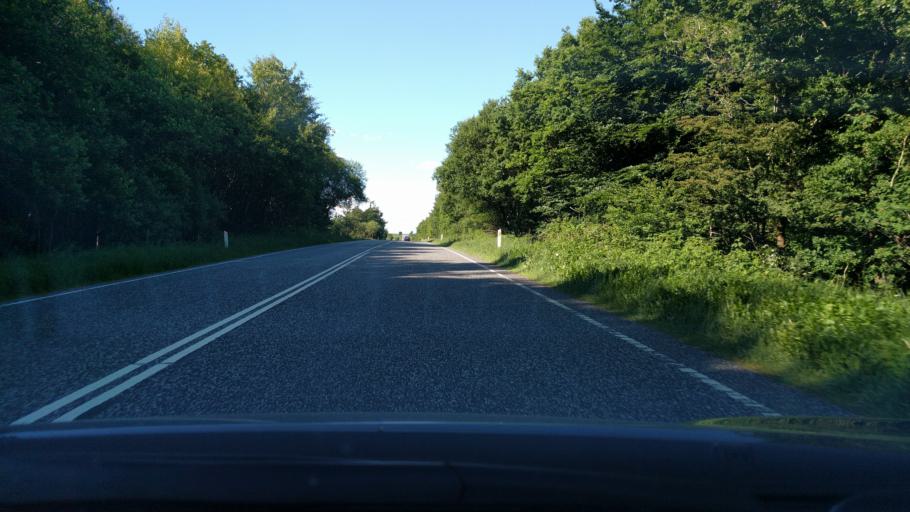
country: DK
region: North Denmark
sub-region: Vesthimmerland Kommune
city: Alestrup
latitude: 56.6371
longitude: 9.5183
